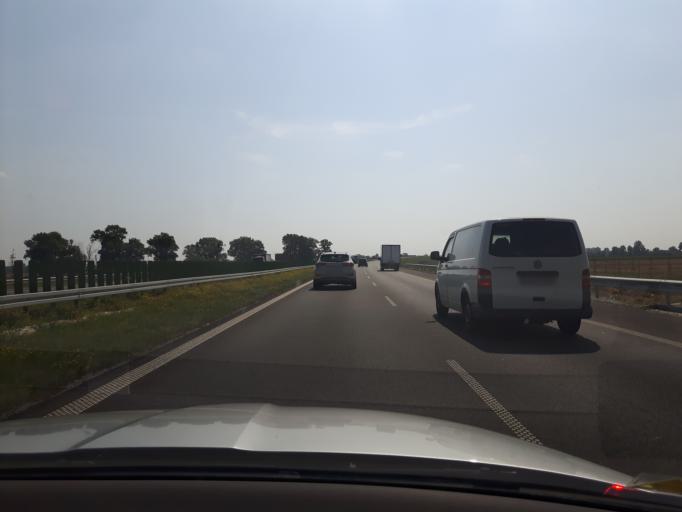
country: PL
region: Pomeranian Voivodeship
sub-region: Powiat nowodworski
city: Nowy Dwor Gdanski
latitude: 54.1863
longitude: 19.1722
